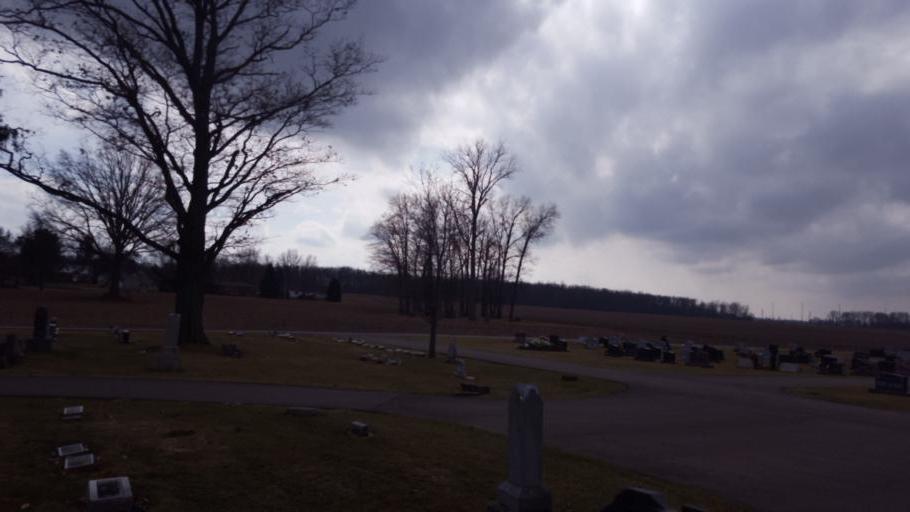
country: US
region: Ohio
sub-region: Richland County
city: Shelby
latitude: 40.8705
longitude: -82.6666
